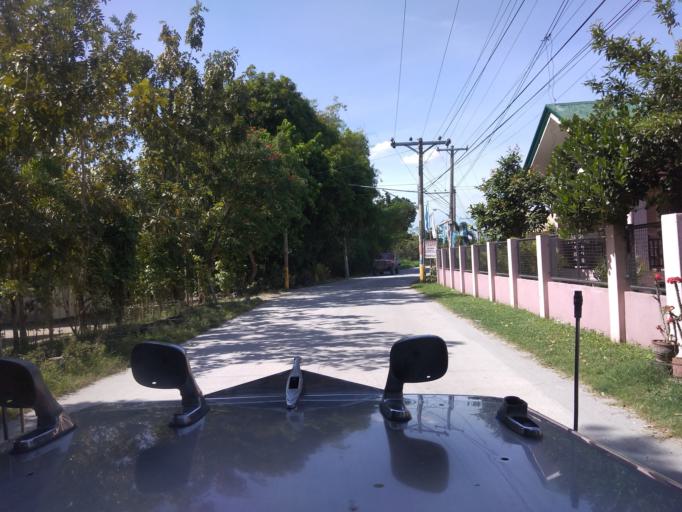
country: PH
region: Central Luzon
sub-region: Province of Pampanga
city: Magliman
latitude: 15.0200
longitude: 120.6563
